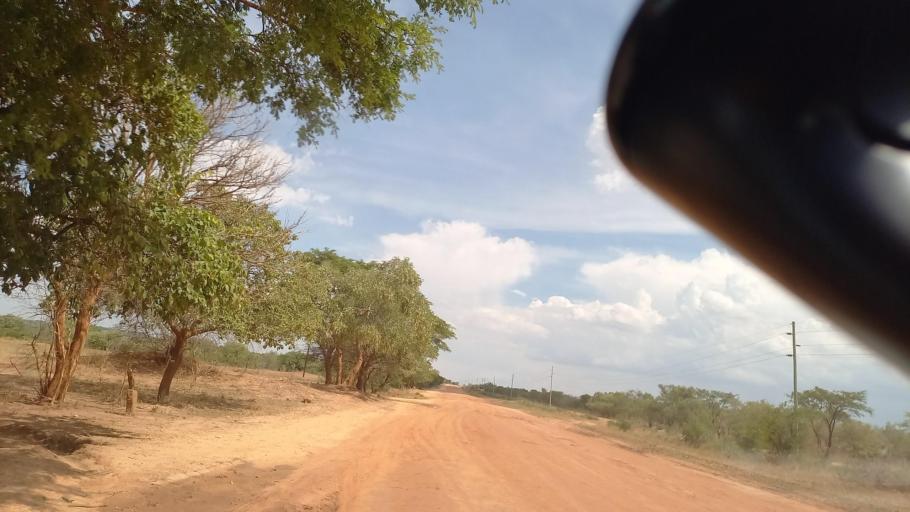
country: ZM
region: Lusaka
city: Kafue
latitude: -16.1388
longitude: 28.0521
